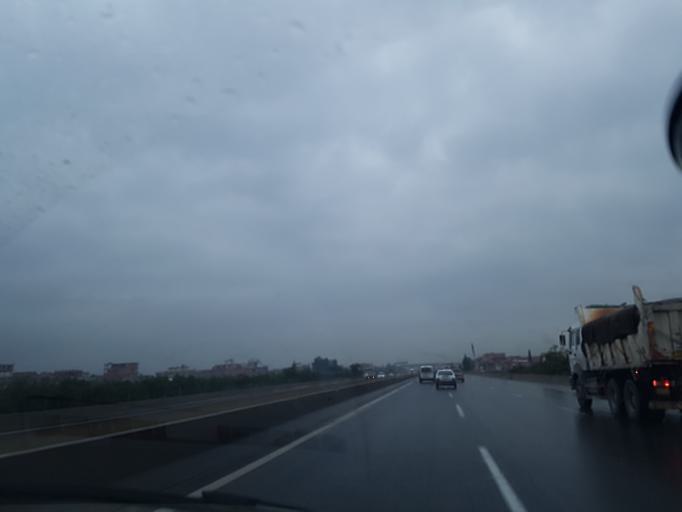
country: DZ
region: Blida
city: Meftah
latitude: 36.6572
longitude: 3.2525
